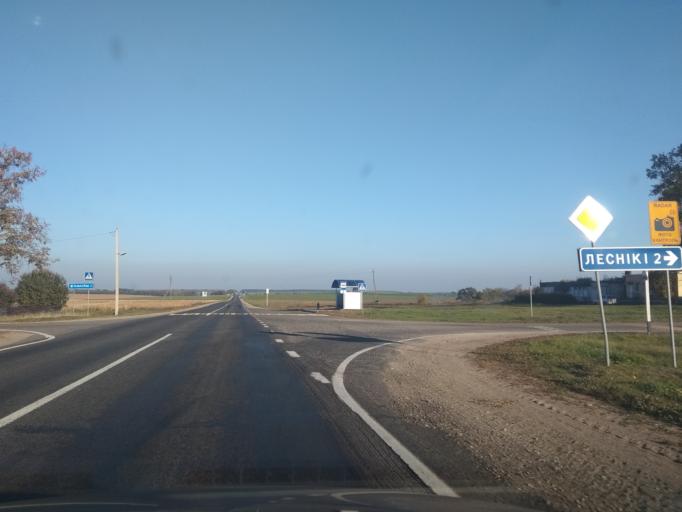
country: BY
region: Grodnenskaya
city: Svislach
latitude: 53.1322
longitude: 24.2006
